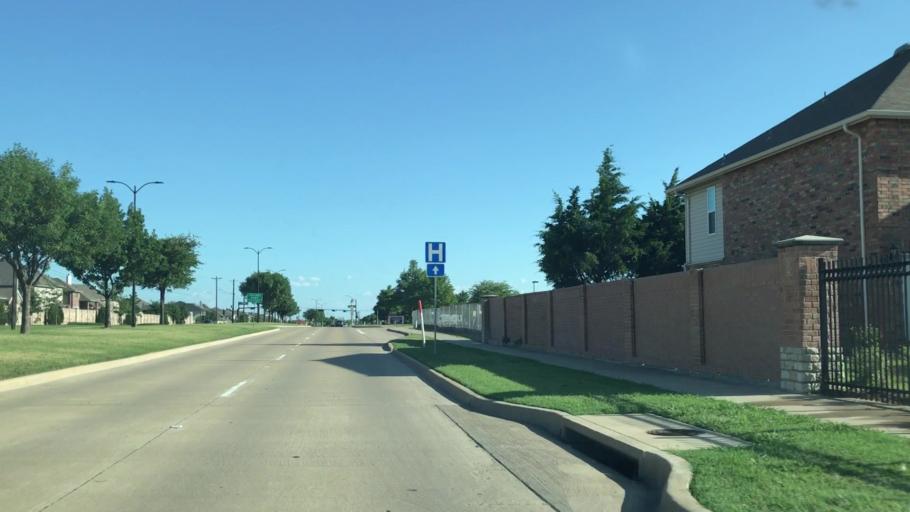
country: US
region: Texas
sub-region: Collin County
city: Frisco
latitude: 33.1329
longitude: -96.7681
